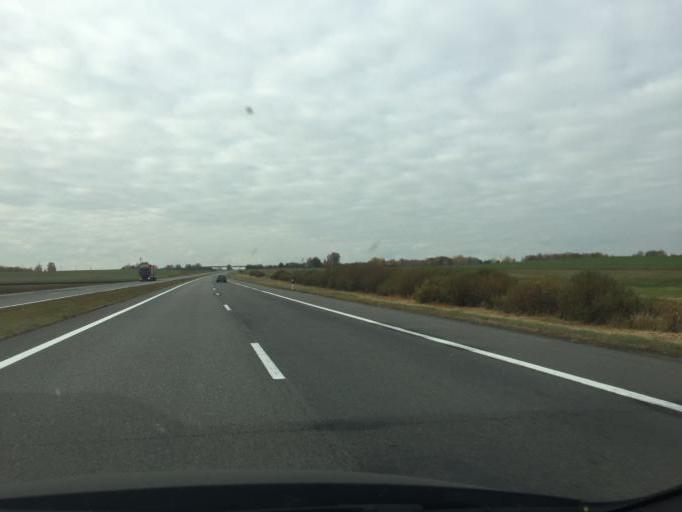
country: BY
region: Minsk
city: Stan'kava
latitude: 53.6758
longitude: 27.2251
